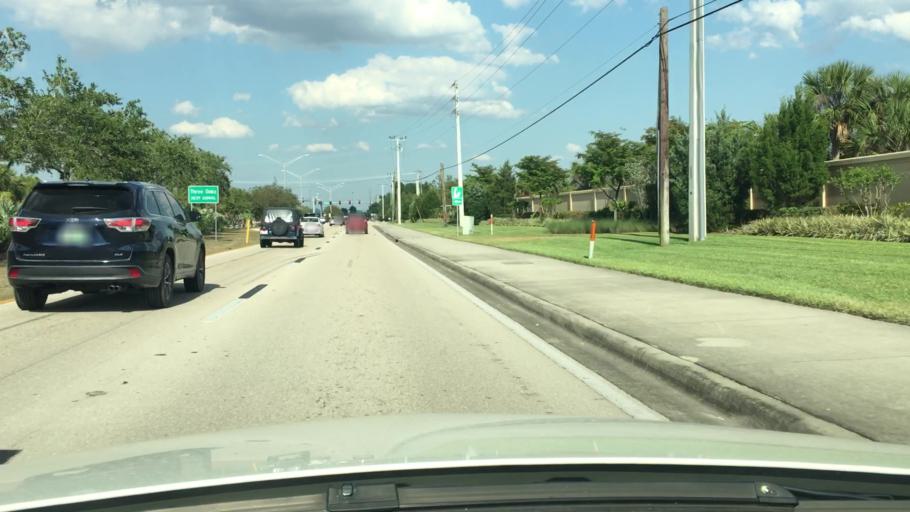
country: US
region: Florida
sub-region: Lee County
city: Estero
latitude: 26.4312
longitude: -81.7914
